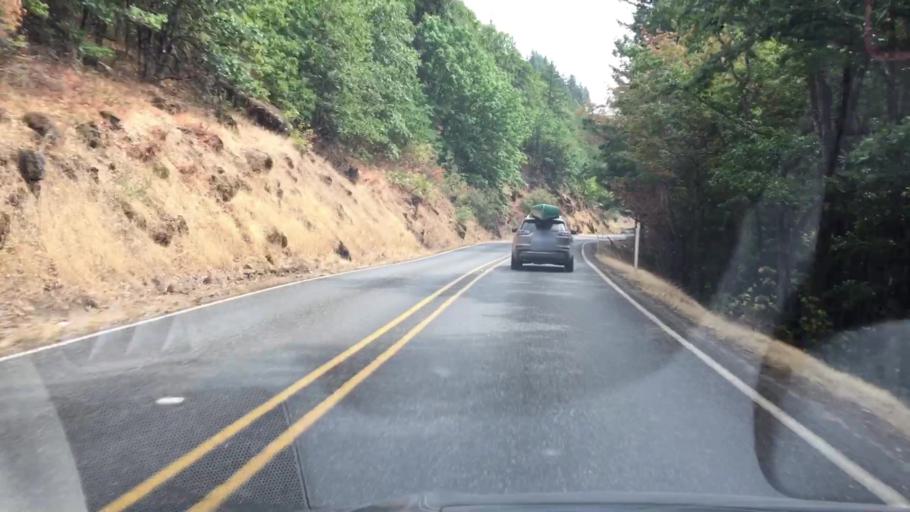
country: US
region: Oregon
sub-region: Hood River County
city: Hood River
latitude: 45.7402
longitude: -121.5219
